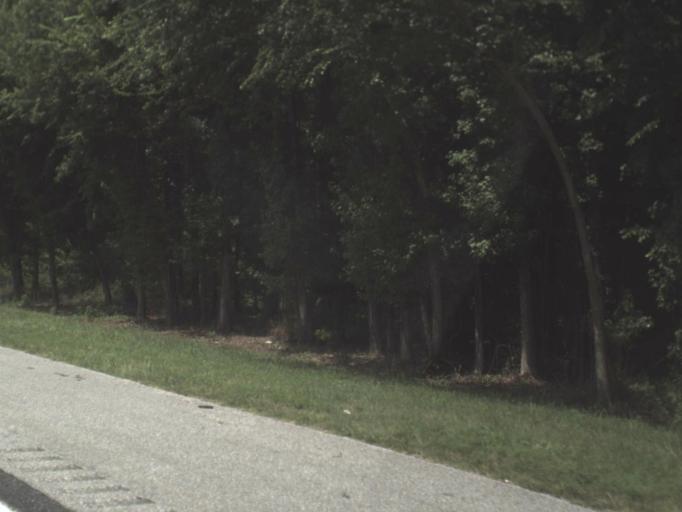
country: US
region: Florida
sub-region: Saint Johns County
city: Palm Valley
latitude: 30.0984
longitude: -81.4994
